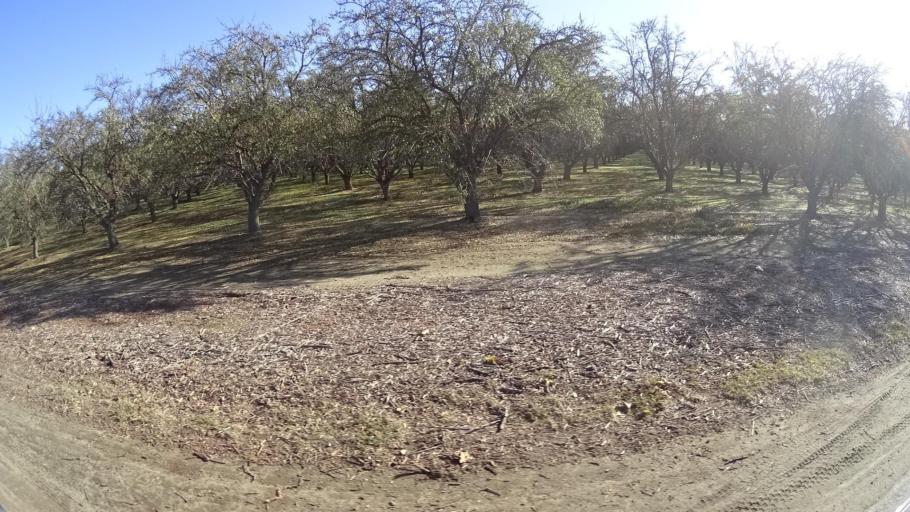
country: US
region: California
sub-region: Kern County
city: McFarland
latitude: 35.6868
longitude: -119.2675
